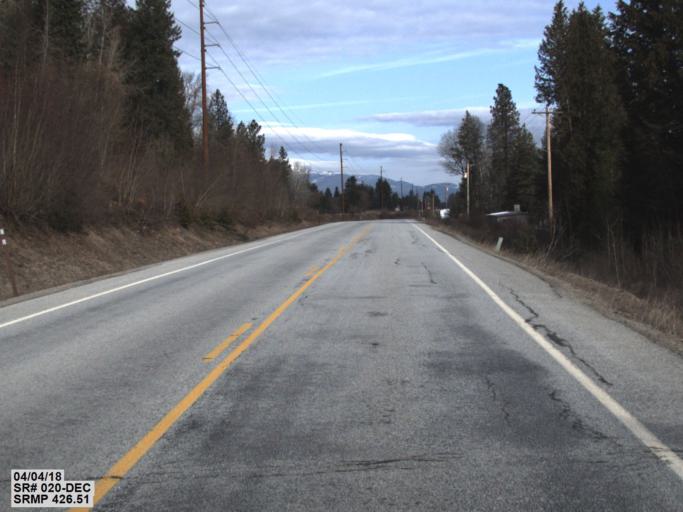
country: US
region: Washington
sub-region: Pend Oreille County
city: Newport
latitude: 48.2413
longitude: -117.2325
